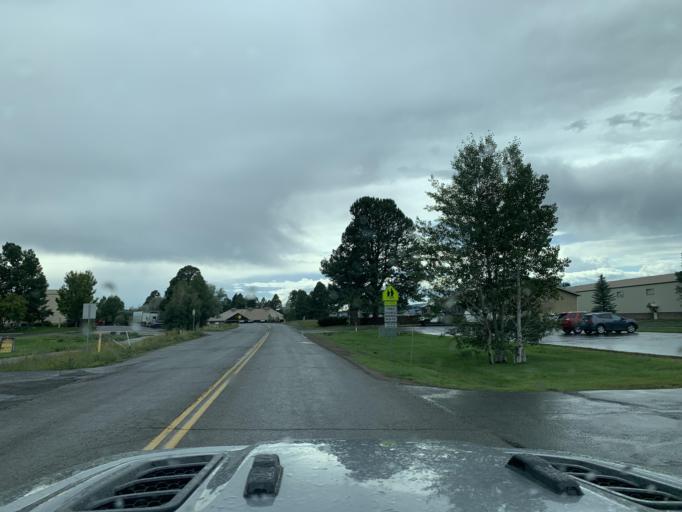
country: US
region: Colorado
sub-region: Archuleta County
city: Pagosa Springs
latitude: 37.2581
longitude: -107.0748
